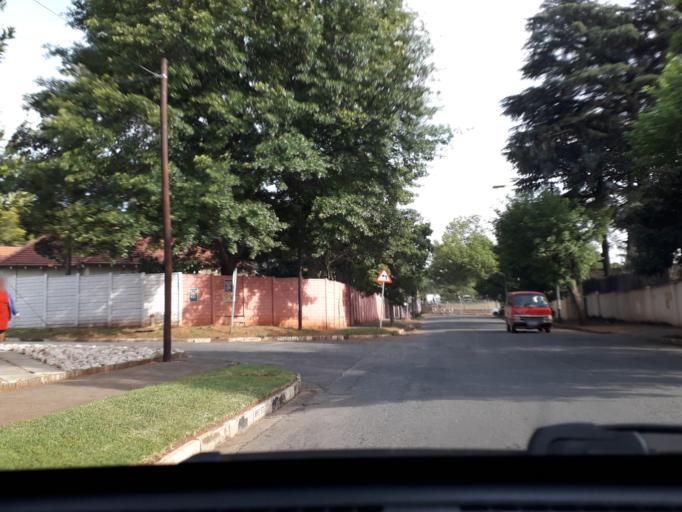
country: ZA
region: Gauteng
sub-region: City of Johannesburg Metropolitan Municipality
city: Johannesburg
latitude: -26.1459
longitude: 28.0952
